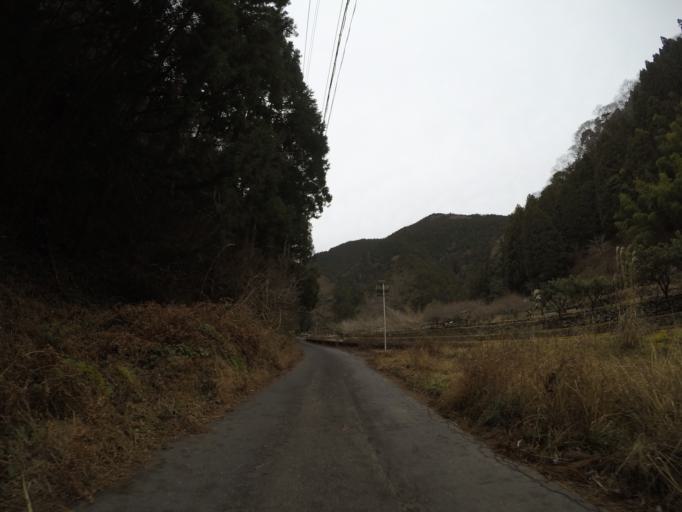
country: JP
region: Shizuoka
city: Fujinomiya
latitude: 35.2840
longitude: 138.5341
